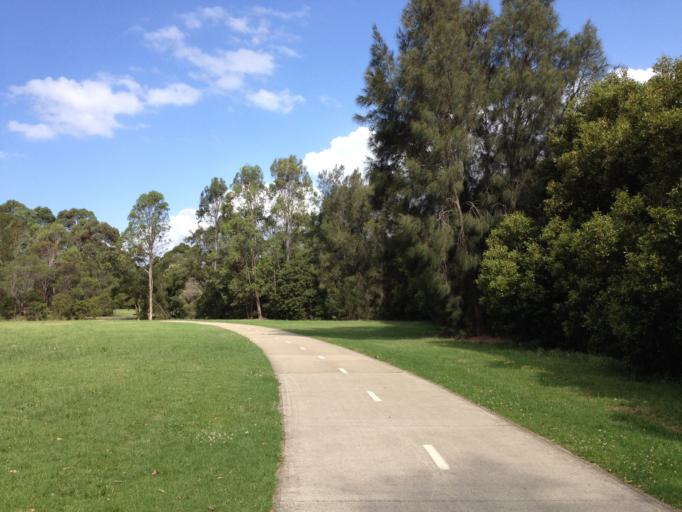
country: AU
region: New South Wales
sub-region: Parramatta
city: Ermington
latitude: -33.8220
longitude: 151.0482
